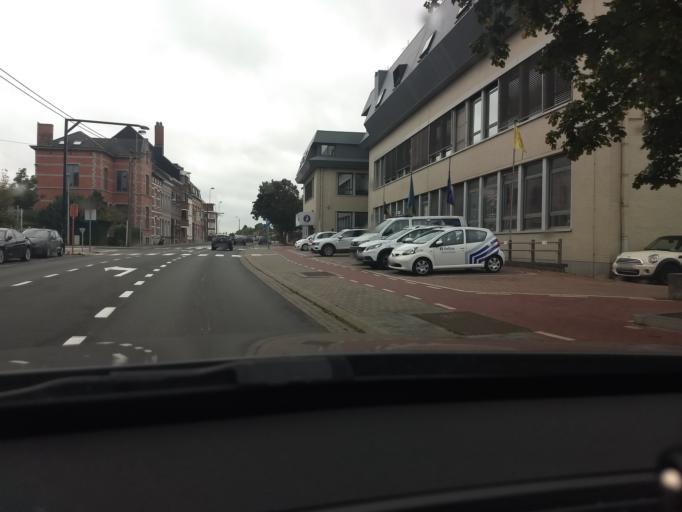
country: BE
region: Wallonia
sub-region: Province du Brabant Wallon
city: Braine-l'Alleud
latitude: 50.6844
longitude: 4.3766
